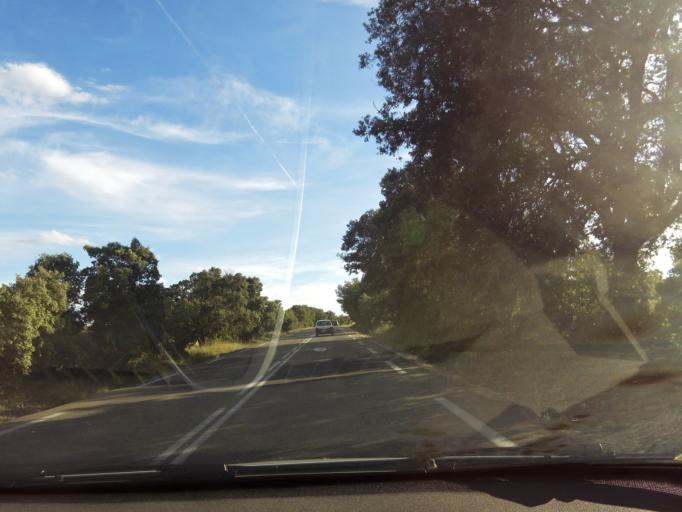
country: FR
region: Languedoc-Roussillon
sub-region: Departement de l'Herault
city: Claret
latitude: 43.8530
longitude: 3.9276
